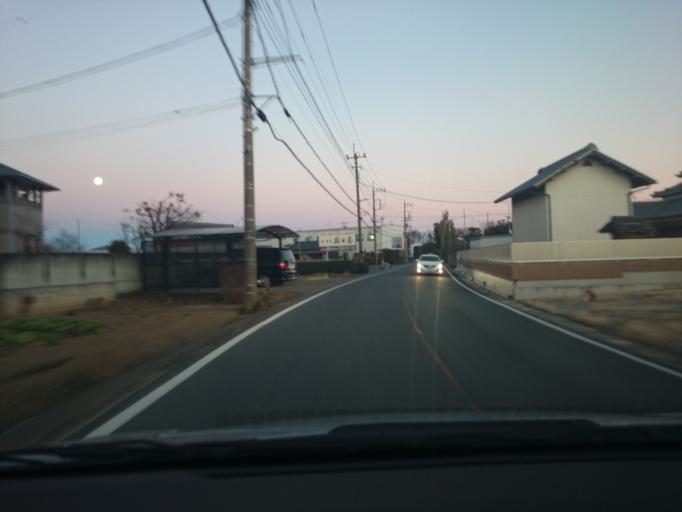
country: JP
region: Saitama
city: Fukayacho
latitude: 36.2299
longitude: 139.2950
